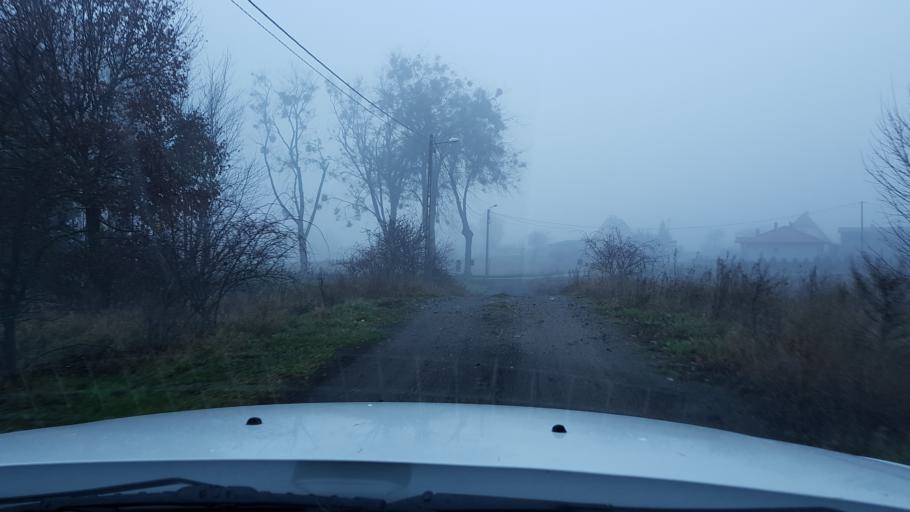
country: PL
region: West Pomeranian Voivodeship
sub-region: Powiat mysliborski
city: Mysliborz
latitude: 52.8996
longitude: 14.8225
